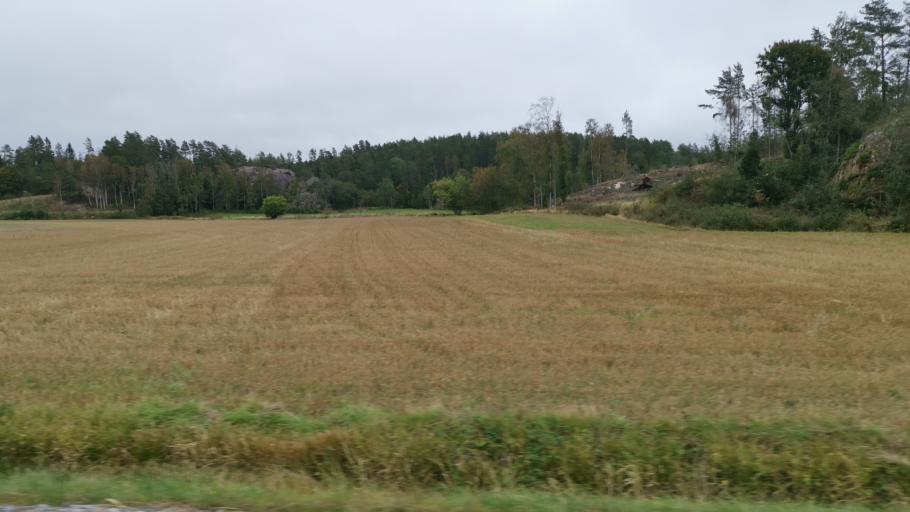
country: SE
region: Vaestra Goetaland
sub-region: Tanums Kommun
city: Tanumshede
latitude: 58.6464
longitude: 11.3389
